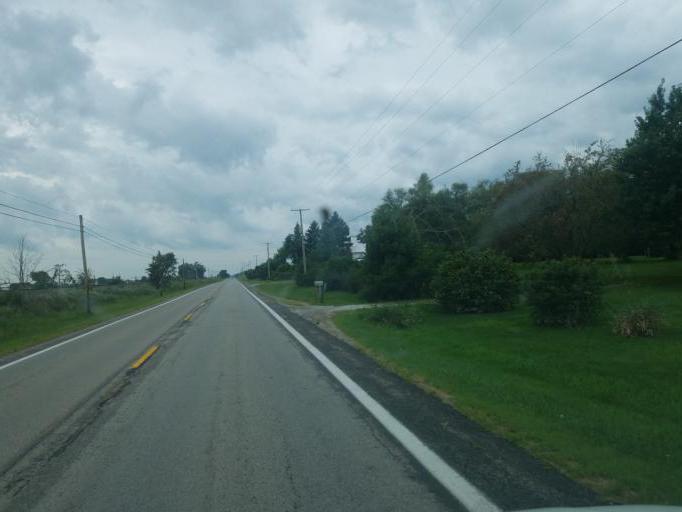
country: US
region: Ohio
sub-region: Delaware County
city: Ashley
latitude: 40.3994
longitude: -82.9619
